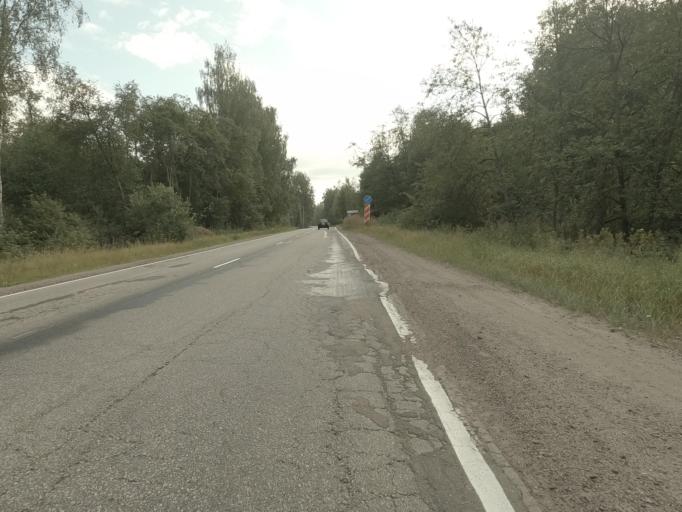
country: RU
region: Leningrad
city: Kamennogorsk
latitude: 60.8640
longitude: 28.9733
